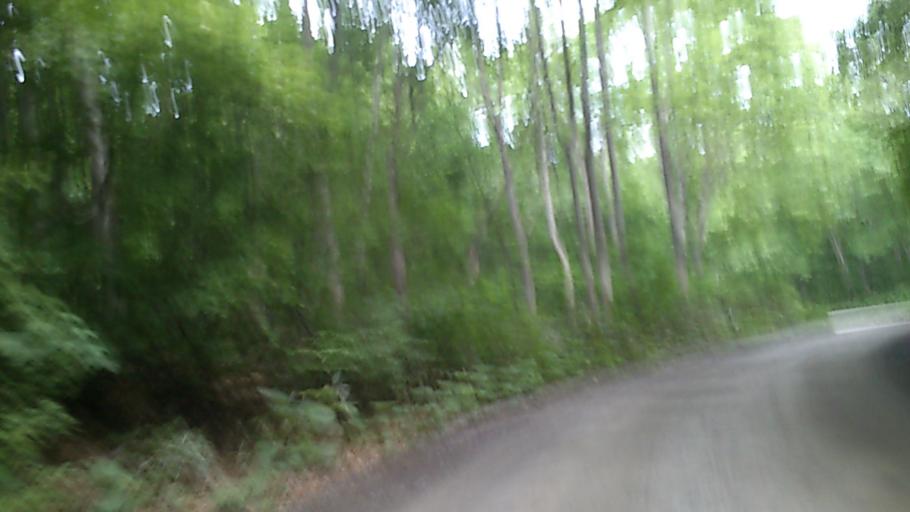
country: JP
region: Aomori
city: Hirosaki
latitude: 40.5637
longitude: 140.1753
